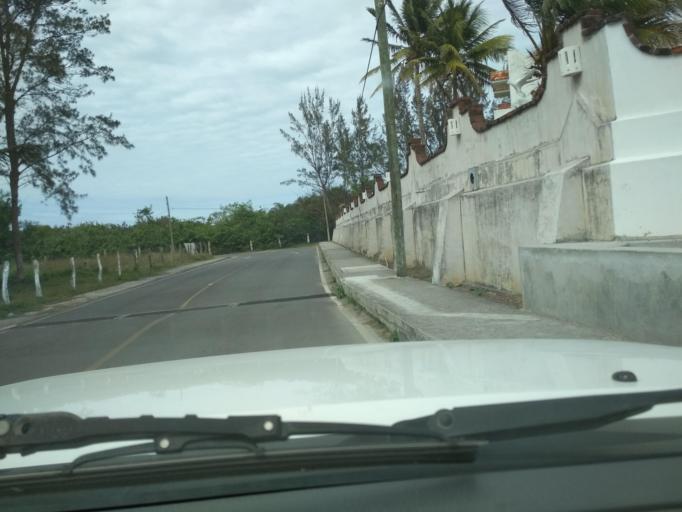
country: MX
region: Veracruz
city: Anton Lizardo
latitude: 19.0392
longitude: -95.9700
